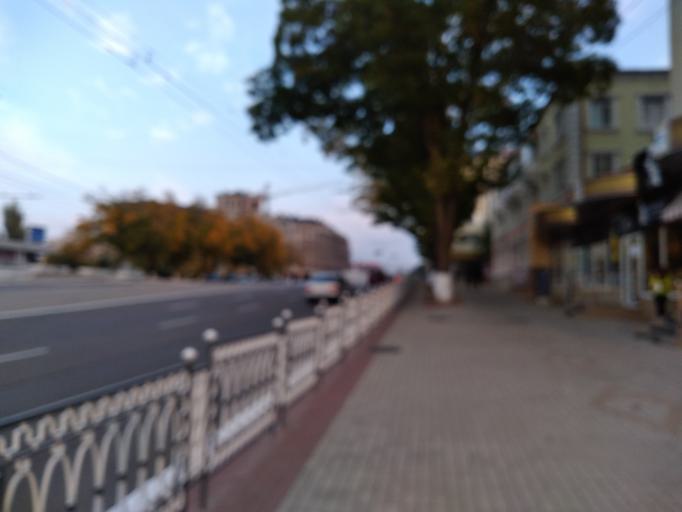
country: MD
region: Telenesti
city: Tiraspolul Nou
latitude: 46.8359
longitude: 29.6130
